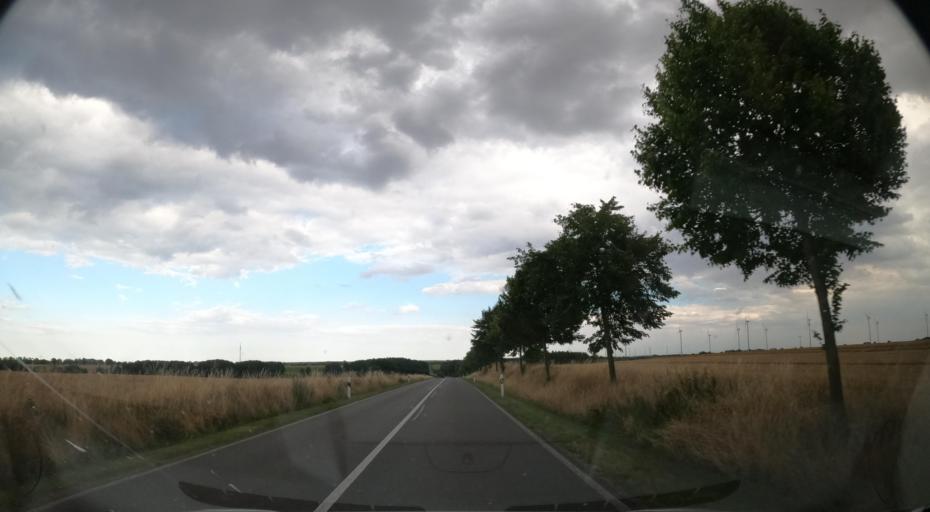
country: DE
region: Mecklenburg-Vorpommern
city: Strasburg
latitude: 53.4882
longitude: 13.8430
